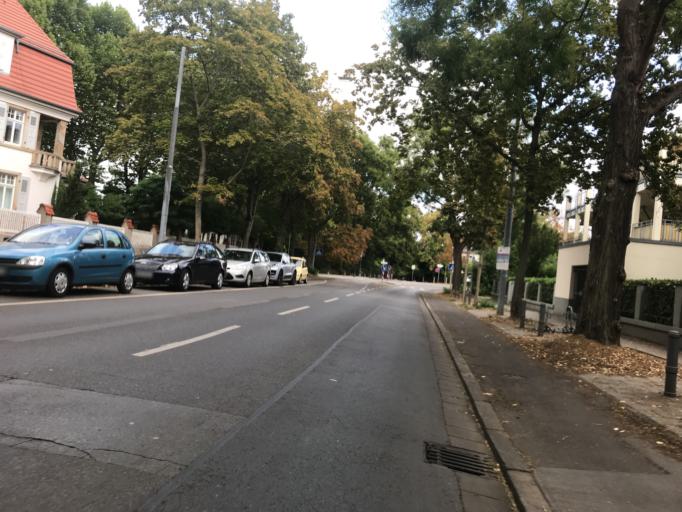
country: DE
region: Rheinland-Pfalz
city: Mainz
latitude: 49.9885
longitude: 8.2831
